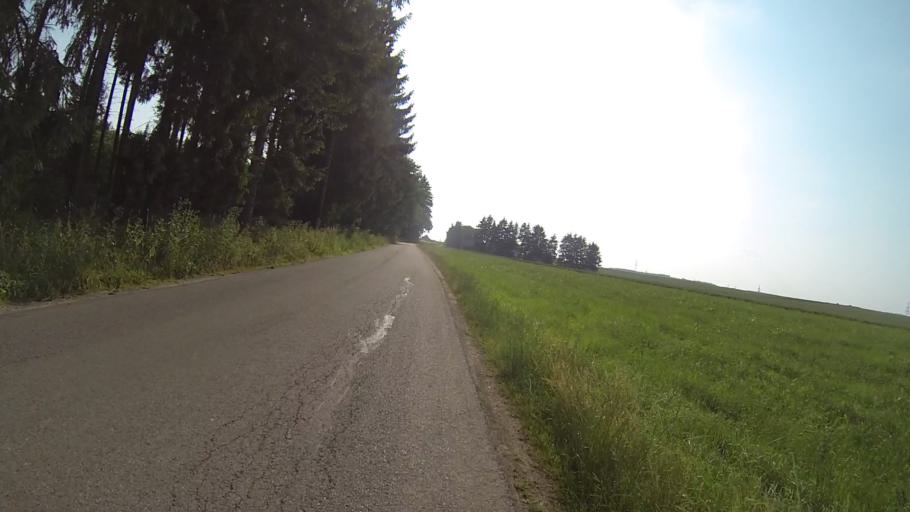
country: DE
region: Baden-Wuerttemberg
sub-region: Tuebingen Region
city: Beimerstetten
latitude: 48.4589
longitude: 10.0051
